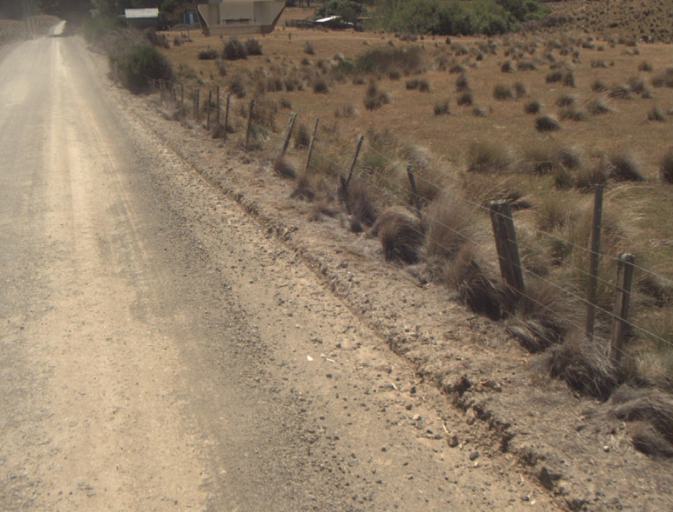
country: AU
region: Tasmania
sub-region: Dorset
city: Scottsdale
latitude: -41.3693
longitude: 147.4700
